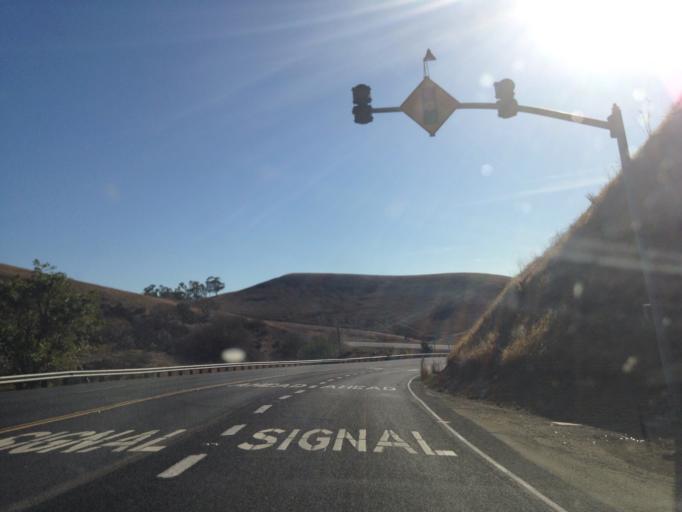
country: US
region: California
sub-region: Contra Costa County
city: Crockett
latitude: 38.0525
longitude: -122.2413
